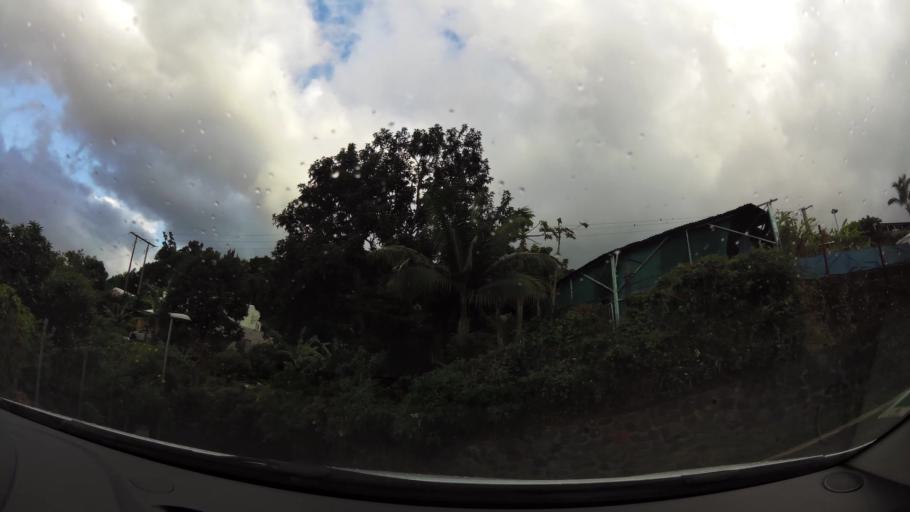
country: RE
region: Reunion
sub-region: Reunion
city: Saint-Denis
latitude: -20.9063
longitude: 55.4408
